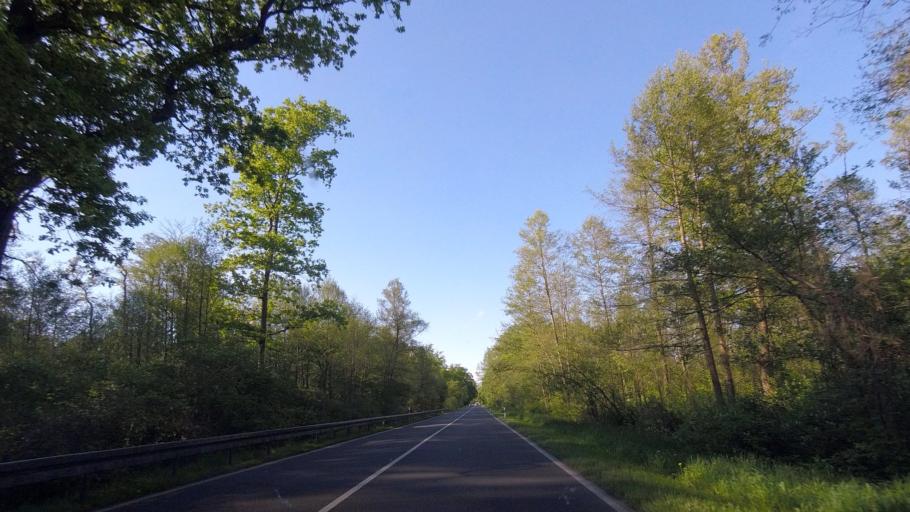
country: DE
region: Brandenburg
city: Luebben
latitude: 51.9018
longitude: 13.8938
